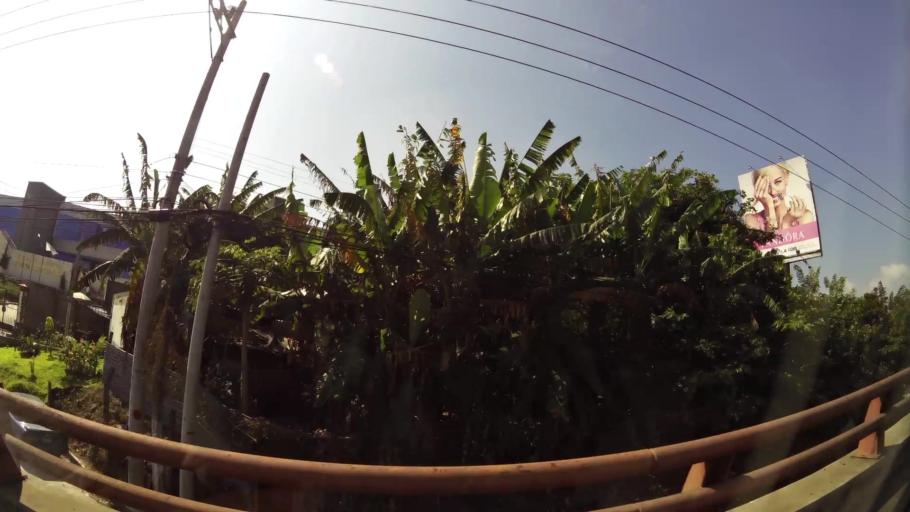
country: SV
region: La Libertad
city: Antiguo Cuscatlan
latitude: 13.6769
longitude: -89.2475
